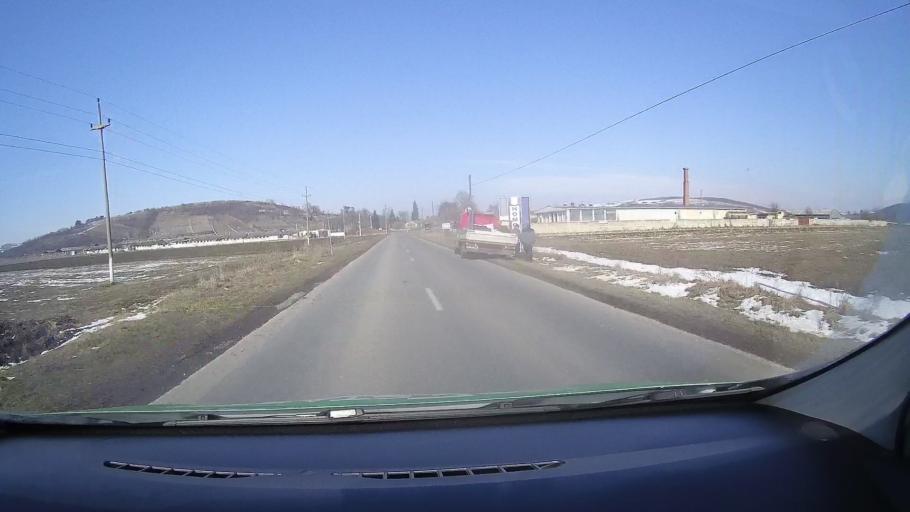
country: RO
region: Brasov
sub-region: Comuna Homorod
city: Homorod
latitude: 46.0333
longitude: 25.2736
